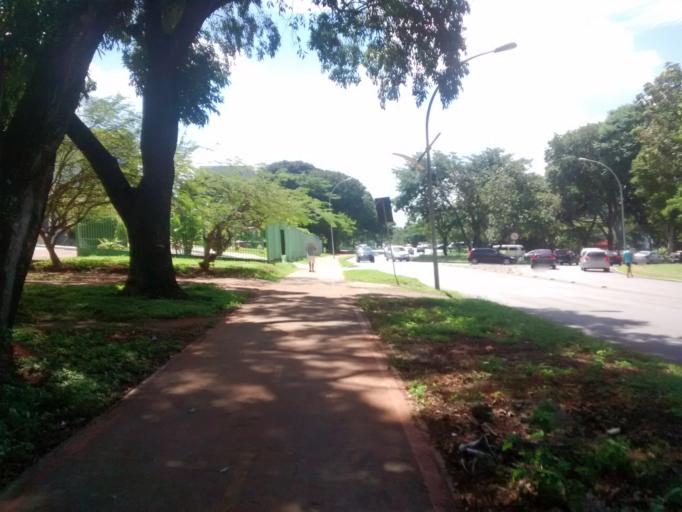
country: BR
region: Federal District
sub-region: Brasilia
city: Brasilia
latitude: -15.7781
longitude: -47.8845
